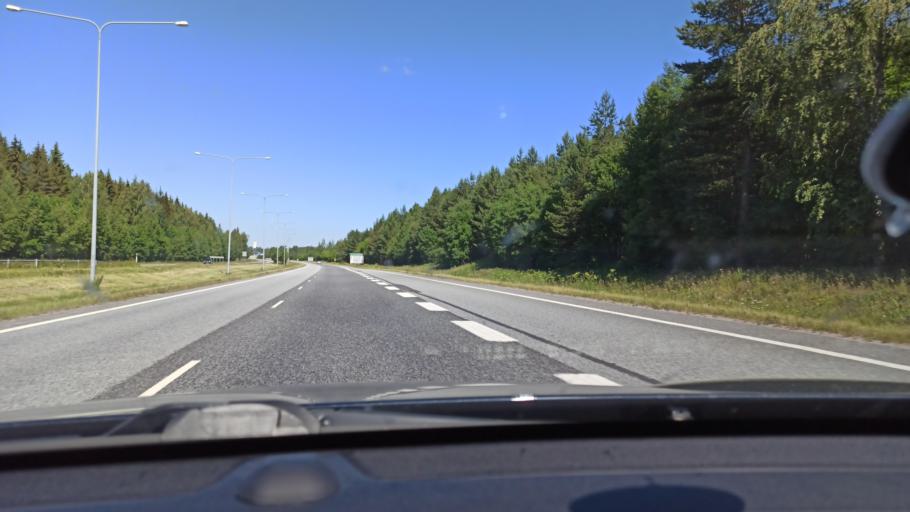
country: FI
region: Ostrobothnia
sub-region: Vaasa
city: Ristinummi
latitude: 63.0584
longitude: 21.7113
